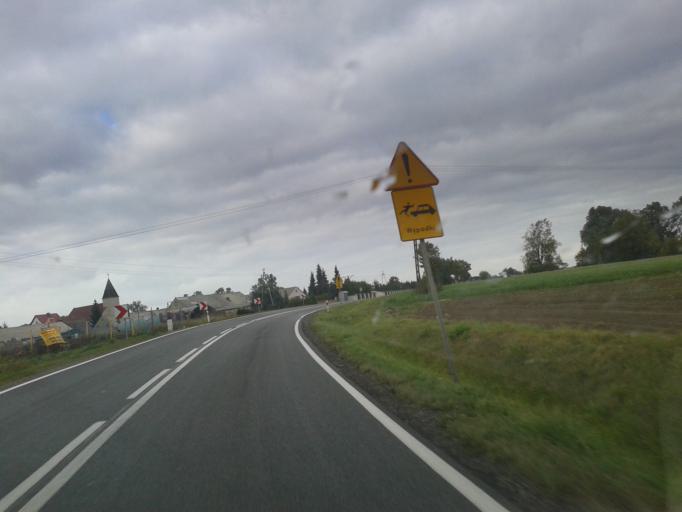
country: PL
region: Kujawsko-Pomorskie
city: Kamien Krajenski
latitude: 53.5000
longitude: 17.5073
